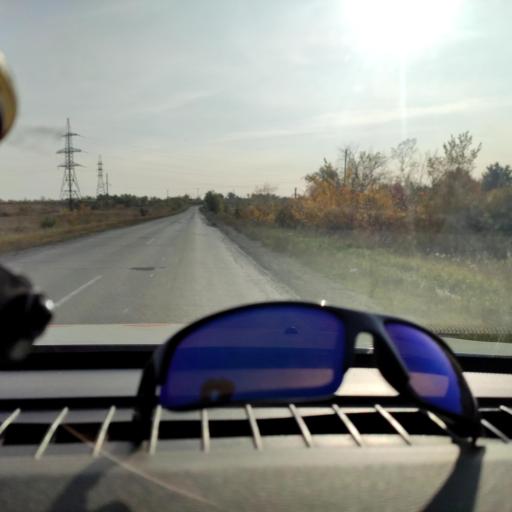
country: RU
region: Samara
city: Chapayevsk
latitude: 53.0012
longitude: 49.7608
